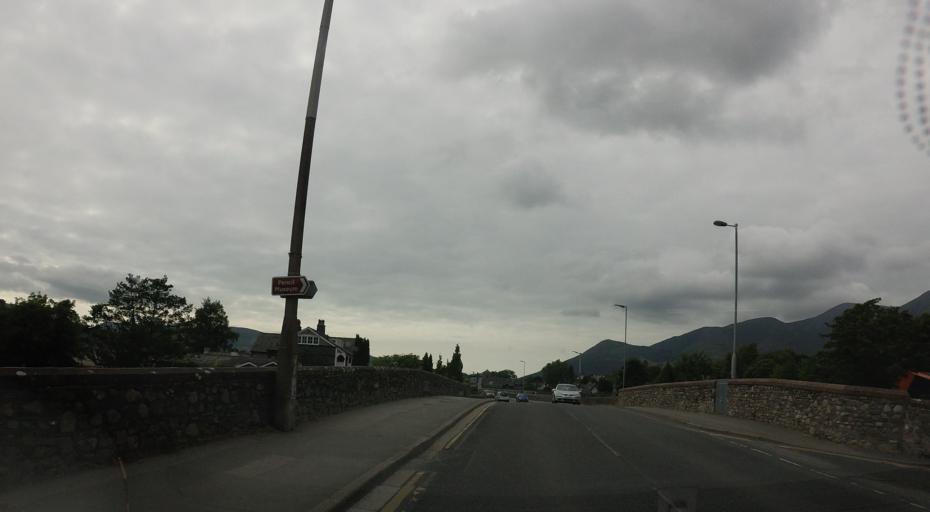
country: GB
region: England
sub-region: Cumbria
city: Keswick
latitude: 54.6032
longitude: -3.1422
